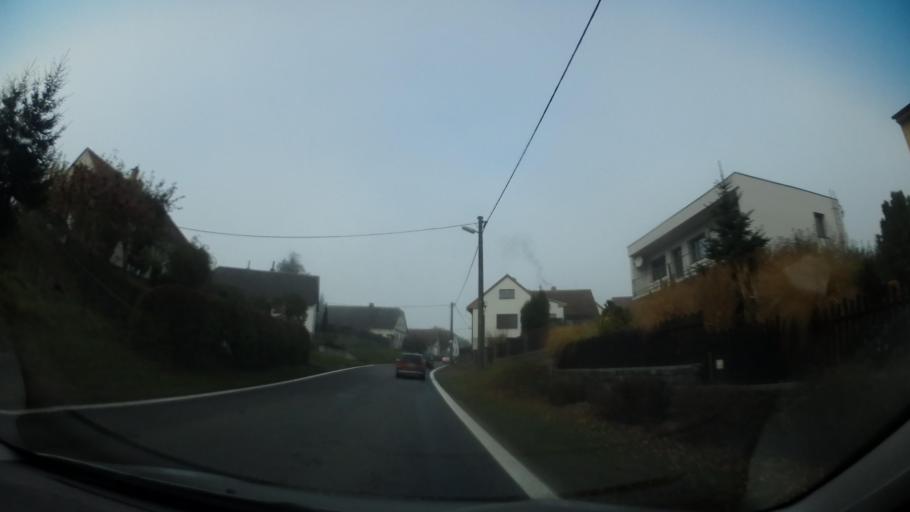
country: CZ
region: Vysocina
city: Krizanov
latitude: 49.4715
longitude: 16.1241
